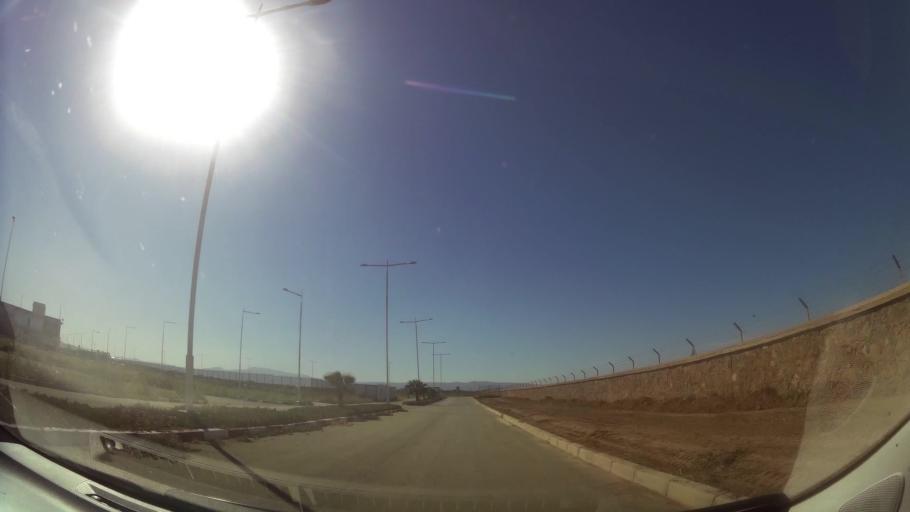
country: MA
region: Oriental
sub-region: Oujda-Angad
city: Oujda
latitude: 34.7759
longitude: -1.9327
